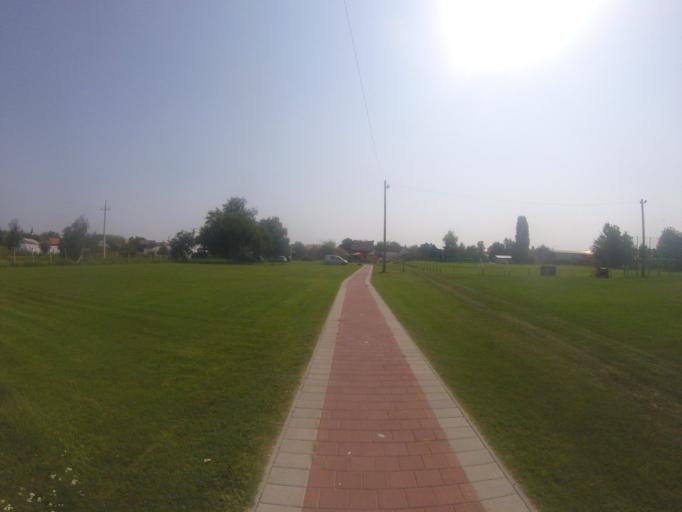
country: HU
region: Bacs-Kiskun
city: Ersekcsanad
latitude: 46.2504
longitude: 18.9741
